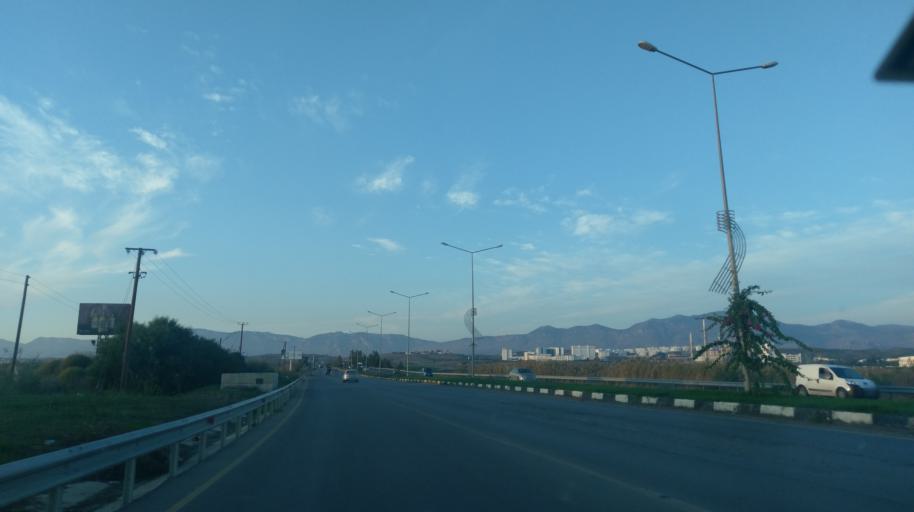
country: CY
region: Lefkosia
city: Nicosia
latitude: 35.2117
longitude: 33.3218
